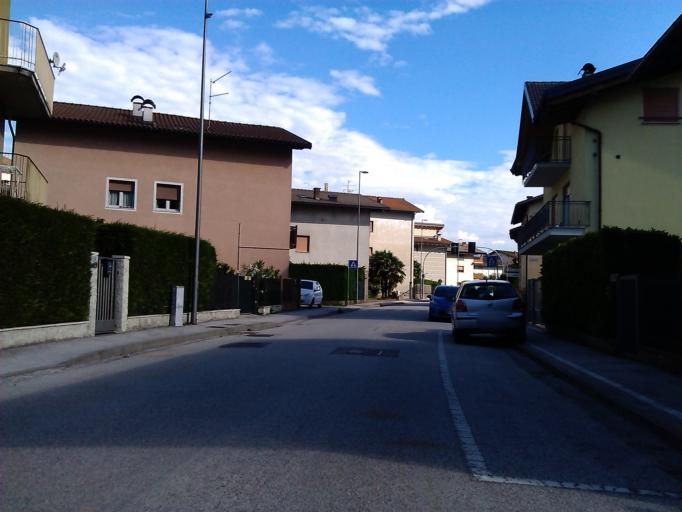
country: IT
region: Trentino-Alto Adige
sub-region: Provincia di Trento
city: Zambana
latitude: 46.1532
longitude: 11.0952
